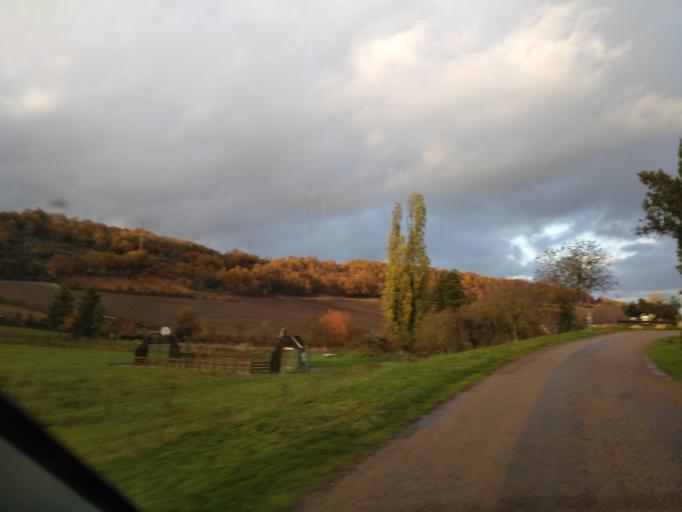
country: FR
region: Bourgogne
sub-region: Departement de Saone-et-Loire
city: Rully
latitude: 46.8902
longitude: 4.7238
